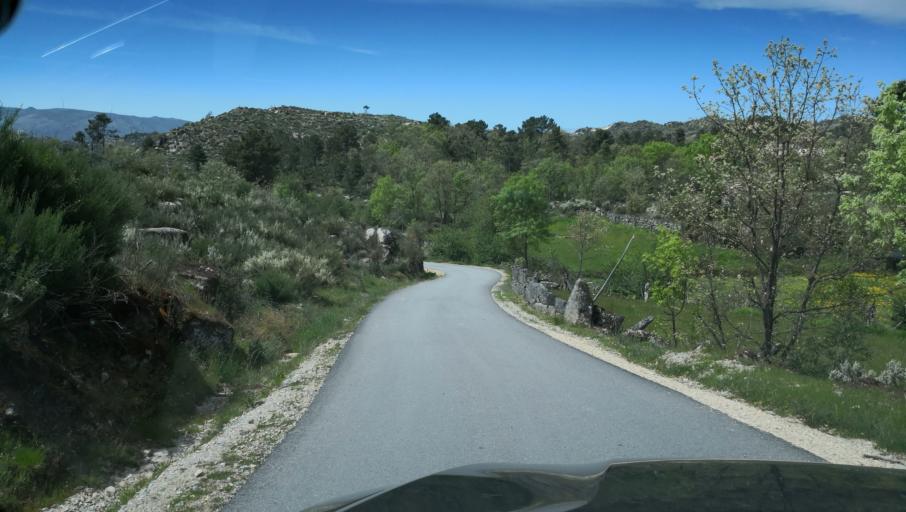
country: PT
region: Vila Real
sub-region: Vila Real
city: Vila Real
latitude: 41.3660
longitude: -7.6696
